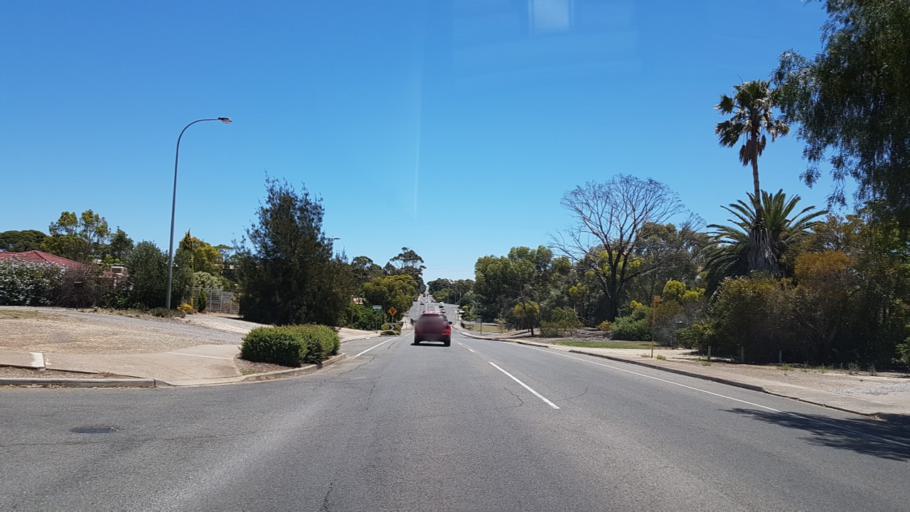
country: AU
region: South Australia
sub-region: Marion
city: Trott Park
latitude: -35.0934
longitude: 138.5505
